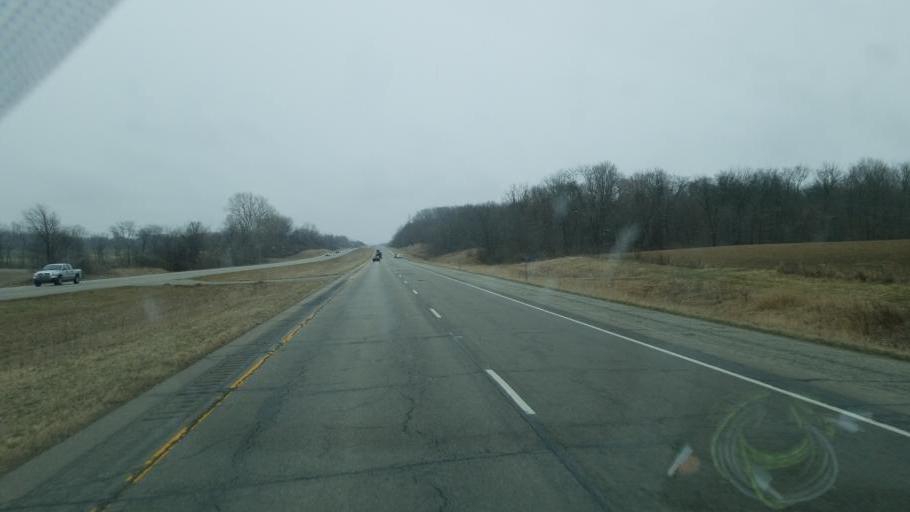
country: US
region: Indiana
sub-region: Wabash County
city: Wabash
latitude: 40.8039
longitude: -85.9076
